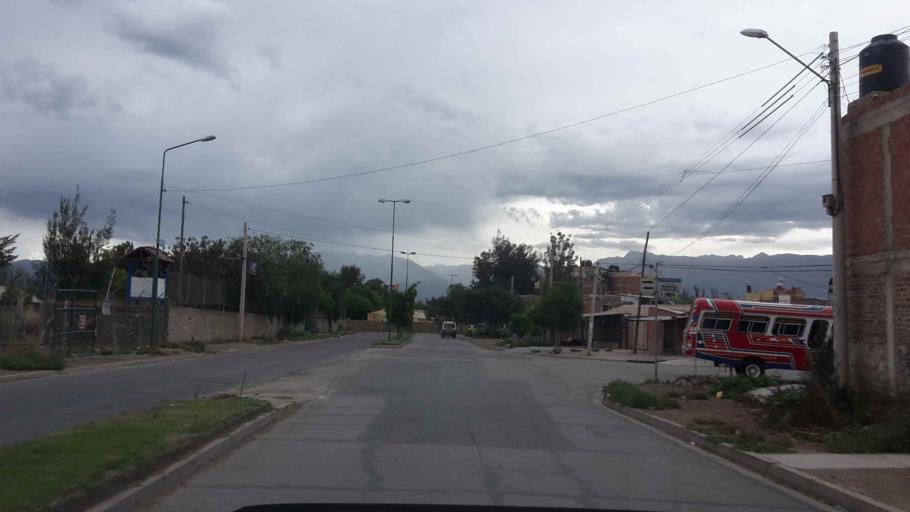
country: BO
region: Cochabamba
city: Cochabamba
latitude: -17.4276
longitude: -66.1651
